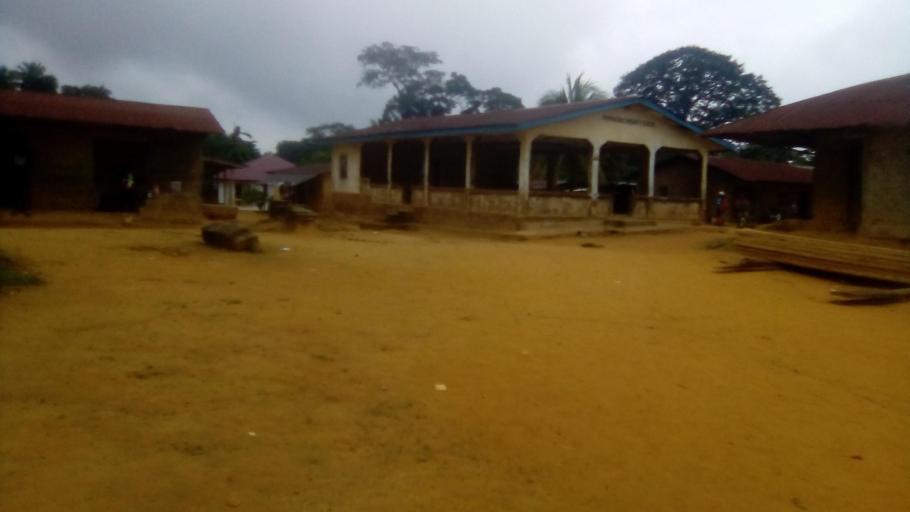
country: SL
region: Eastern Province
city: Kailahun
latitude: 8.2952
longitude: -10.6073
